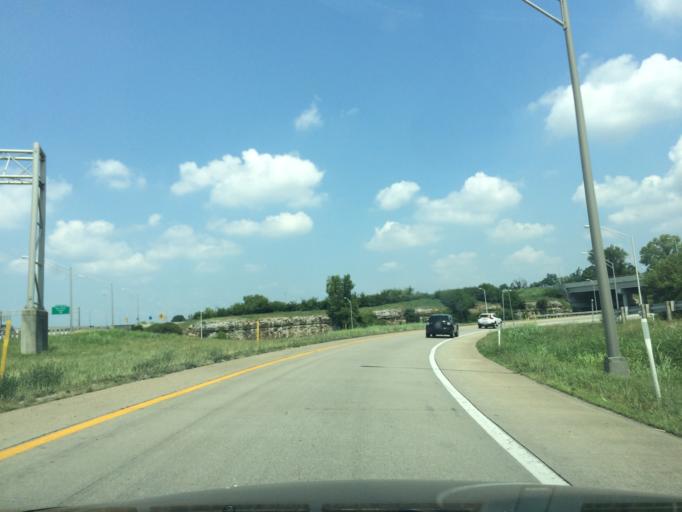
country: US
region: Kentucky
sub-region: Jefferson County
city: Audubon Park
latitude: 38.1879
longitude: -85.7262
